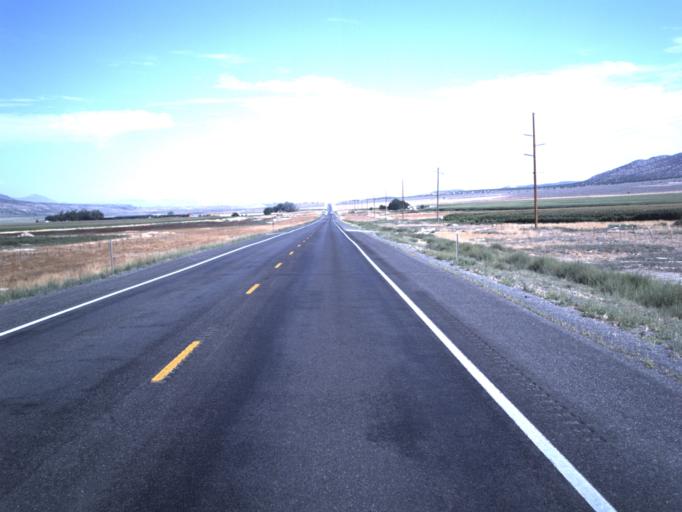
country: US
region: Utah
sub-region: Sanpete County
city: Gunnison
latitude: 39.2519
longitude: -111.8587
